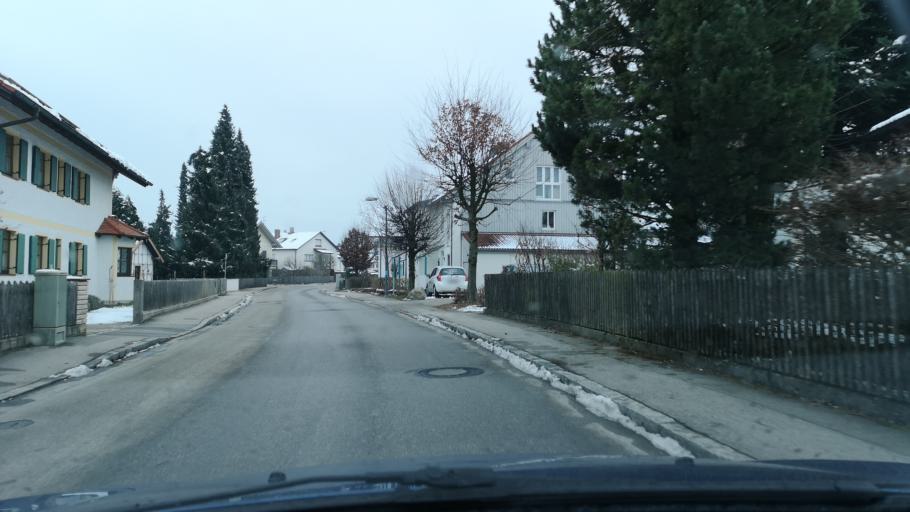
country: DE
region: Bavaria
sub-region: Upper Bavaria
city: Anzing
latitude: 48.1489
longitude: 11.8541
